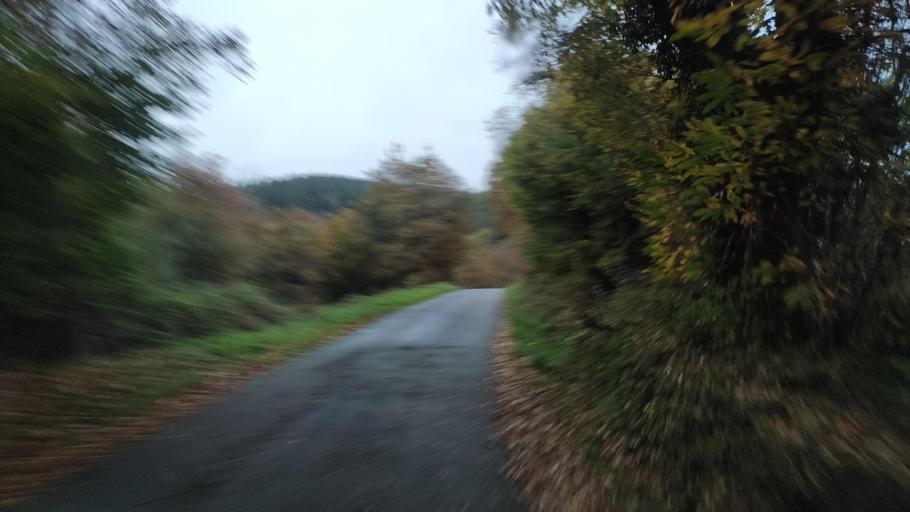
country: FR
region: Limousin
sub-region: Departement de la Haute-Vienne
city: Ambazac
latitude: 46.0007
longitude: 1.4642
